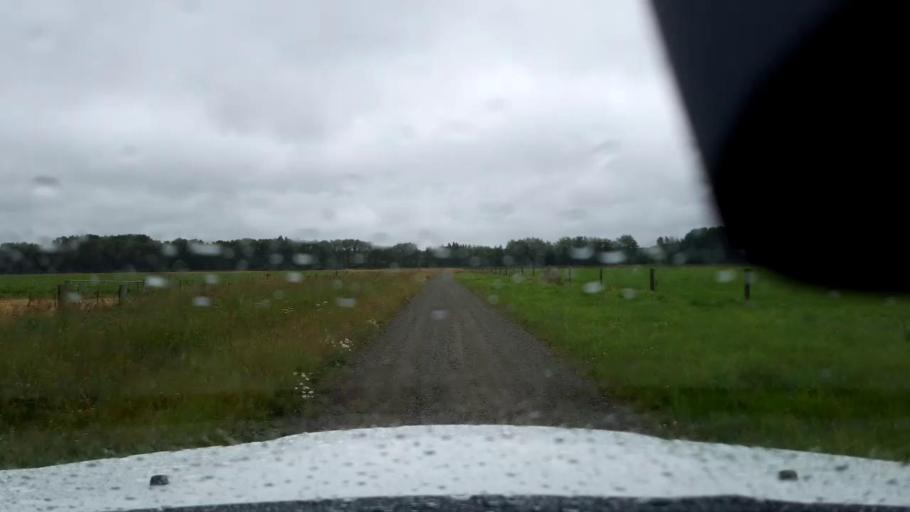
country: NZ
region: Canterbury
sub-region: Timaru District
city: Pleasant Point
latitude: -44.2550
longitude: 171.1997
